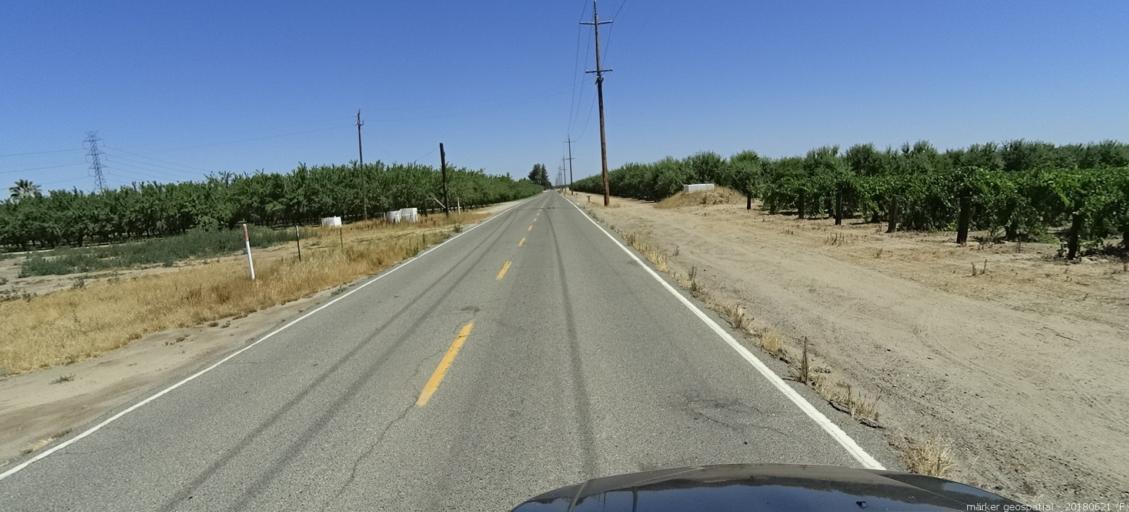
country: US
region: California
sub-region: Madera County
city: Bonadelle Ranchos-Madera Ranchos
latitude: 36.8690
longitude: -119.9113
